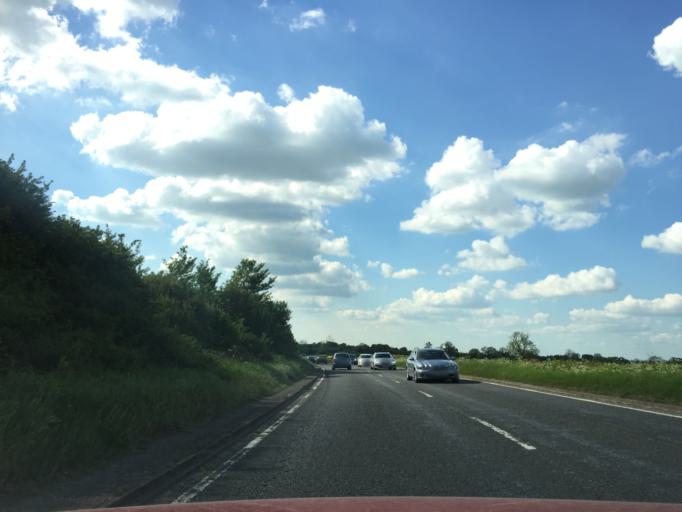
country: GB
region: England
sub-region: Milton Keynes
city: Stony Stratford
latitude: 52.0832
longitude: -0.8641
